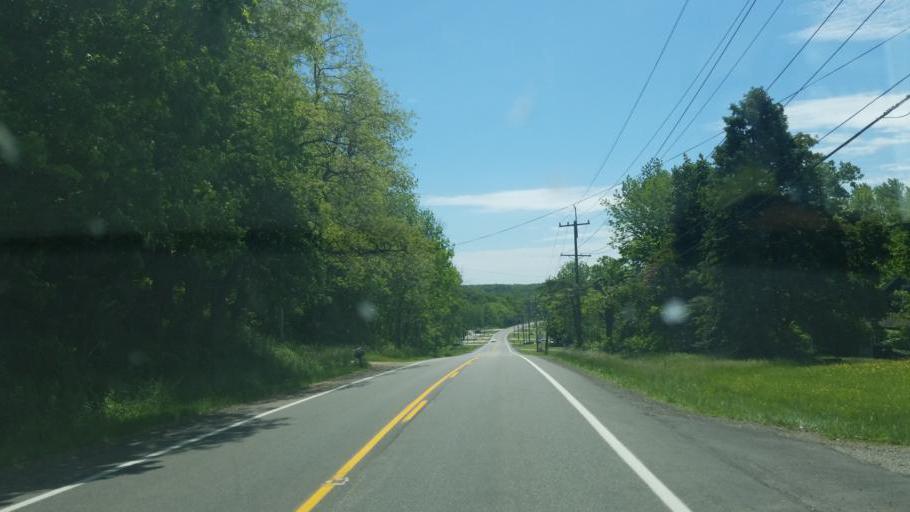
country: US
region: Ohio
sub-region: Geauga County
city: Burton
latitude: 41.4699
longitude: -81.1341
